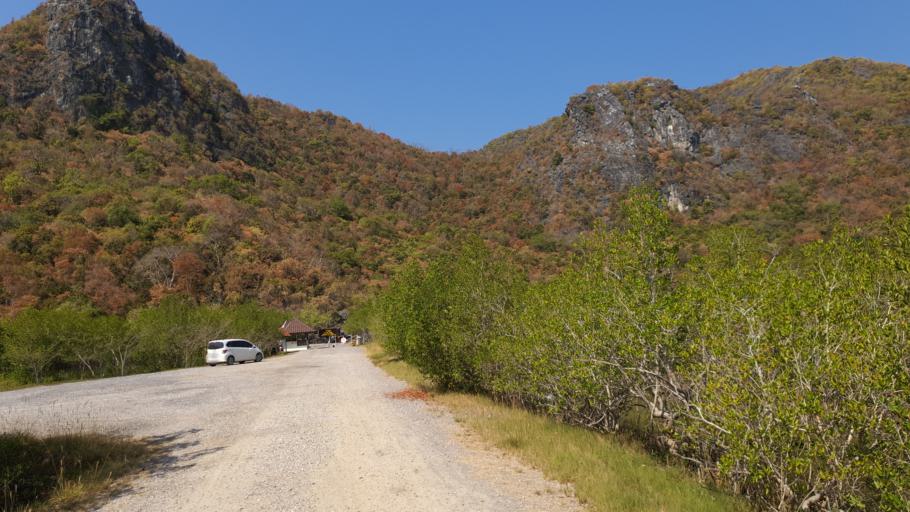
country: TH
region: Prachuap Khiri Khan
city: Sam Roi Yot
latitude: 12.2021
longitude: 99.9929
